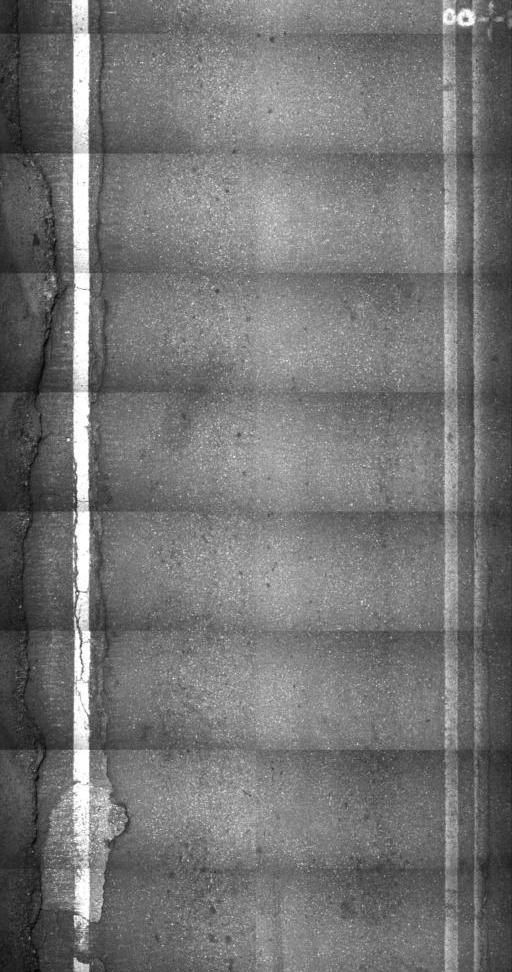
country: US
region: Vermont
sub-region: Orange County
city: Randolph
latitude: 44.0109
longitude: -72.8486
